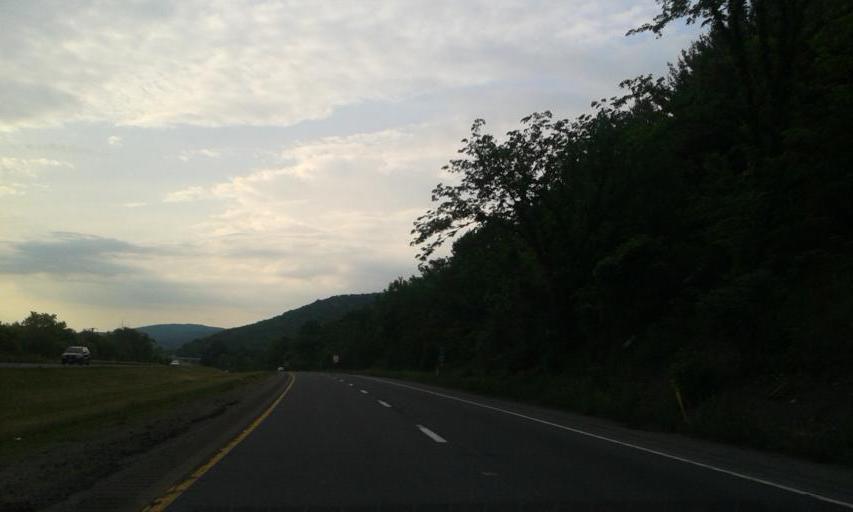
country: US
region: Pennsylvania
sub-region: Susquehanna County
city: Hallstead
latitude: 41.9733
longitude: -75.7406
